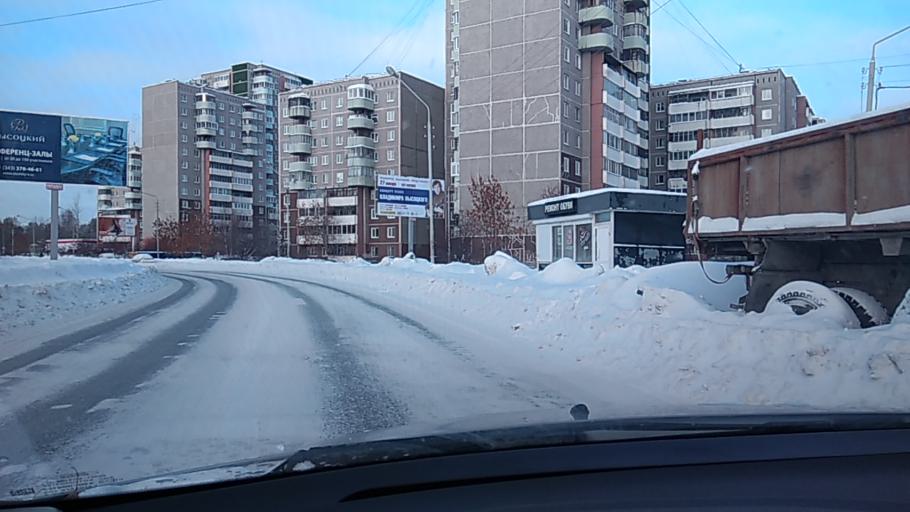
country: RU
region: Sverdlovsk
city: Yekaterinburg
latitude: 56.7920
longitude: 60.6114
